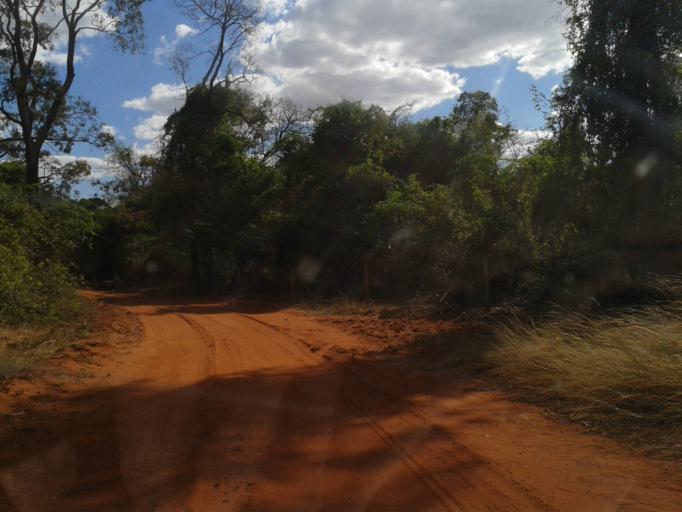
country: BR
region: Minas Gerais
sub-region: Centralina
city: Centralina
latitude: -18.7565
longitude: -49.0794
